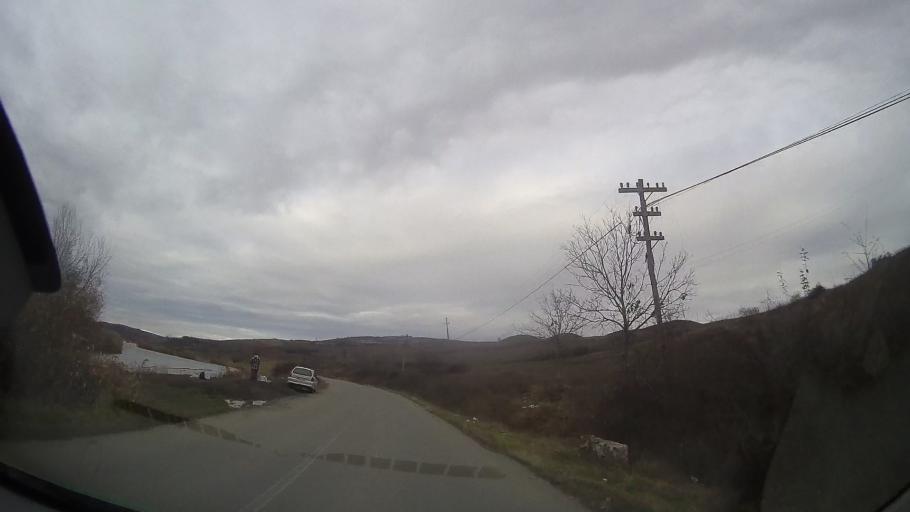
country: RO
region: Mures
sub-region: Comuna Faragau
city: Faragau
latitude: 46.7460
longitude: 24.5315
